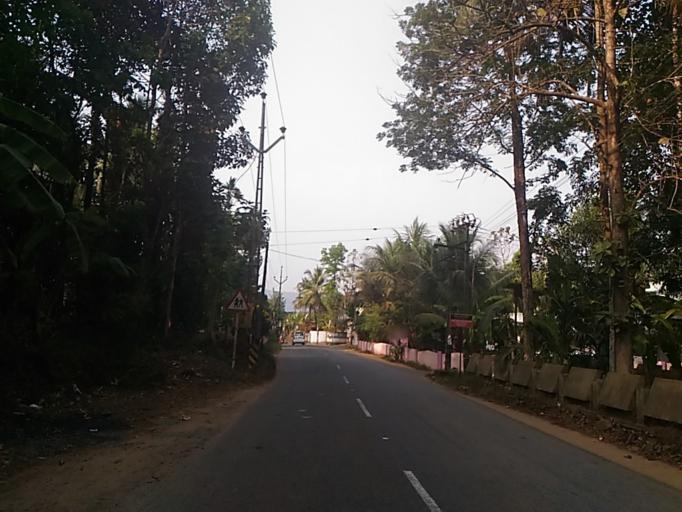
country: IN
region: Kerala
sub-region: Kottayam
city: Palackattumala
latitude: 9.7911
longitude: 76.6631
